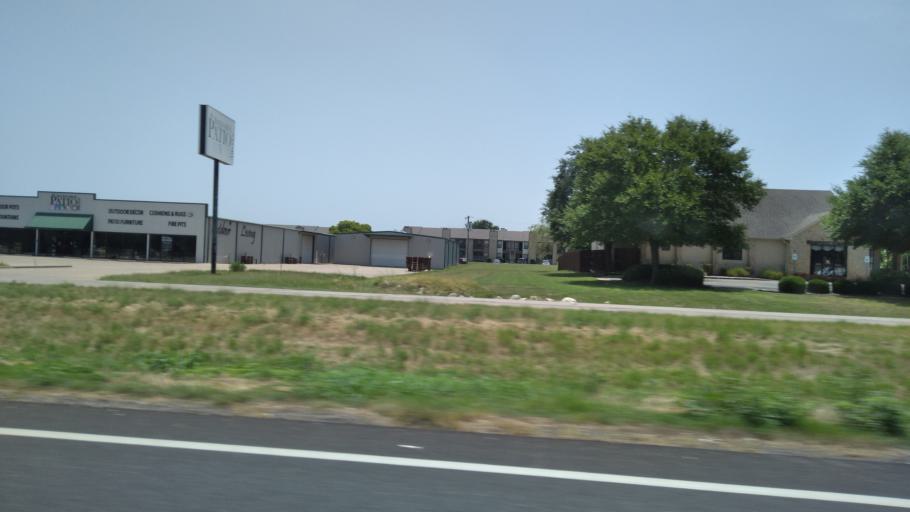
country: US
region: Texas
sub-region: McLennan County
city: Woodway
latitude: 31.5014
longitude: -97.2106
